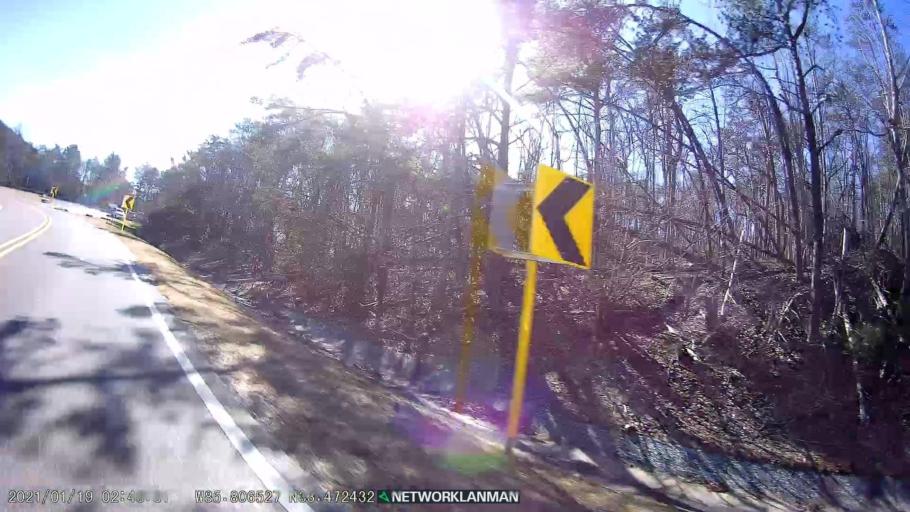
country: US
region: Alabama
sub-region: Calhoun County
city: Oxford
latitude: 33.4723
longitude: -85.8064
